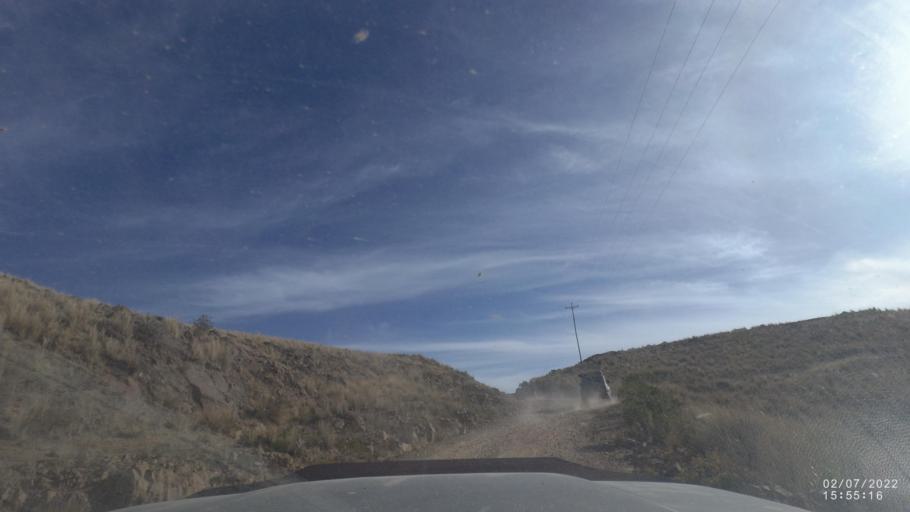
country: BO
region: Cochabamba
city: Irpa Irpa
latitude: -17.9092
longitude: -66.4203
